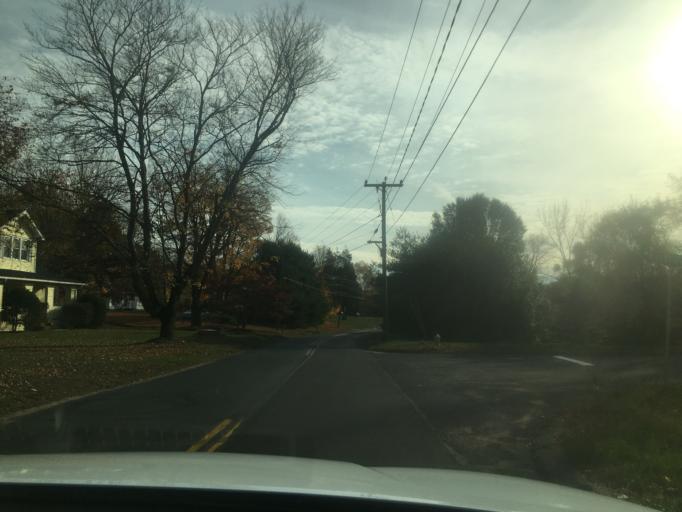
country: US
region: Connecticut
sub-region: Hartford County
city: Broad Brook
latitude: 41.8690
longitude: -72.5715
